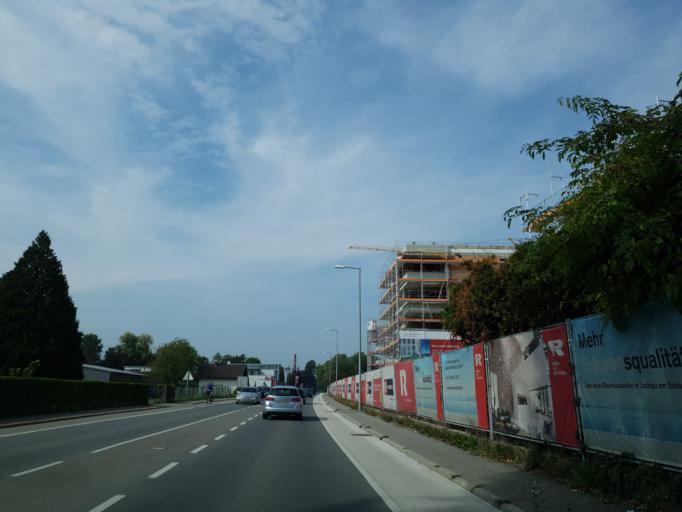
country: AT
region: Vorarlberg
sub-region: Politischer Bezirk Bregenz
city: Lochau
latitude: 47.5309
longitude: 9.7420
